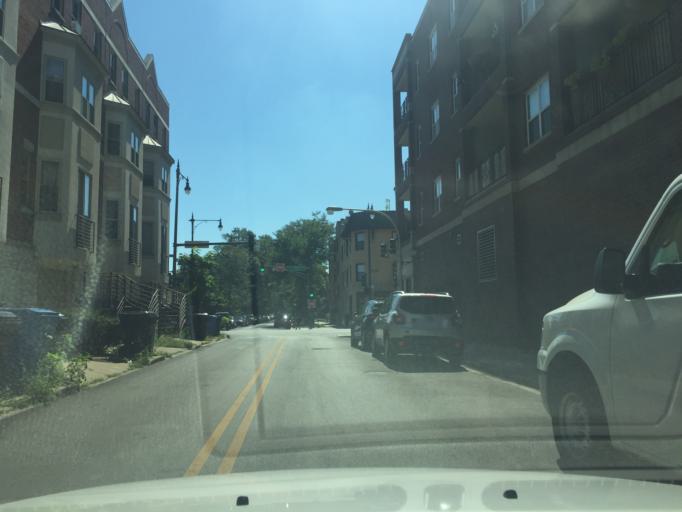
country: US
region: Illinois
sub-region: Cook County
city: Lincolnwood
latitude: 41.9689
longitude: -87.7037
